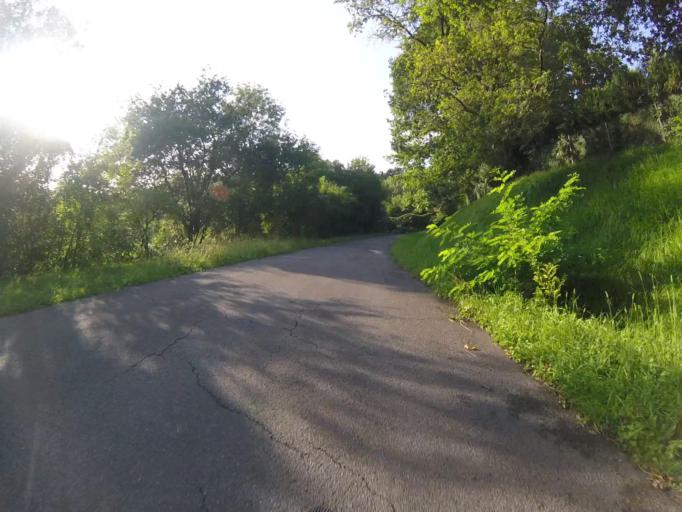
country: ES
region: Basque Country
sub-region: Provincia de Guipuzcoa
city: Irun
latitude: 43.3412
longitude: -1.8386
